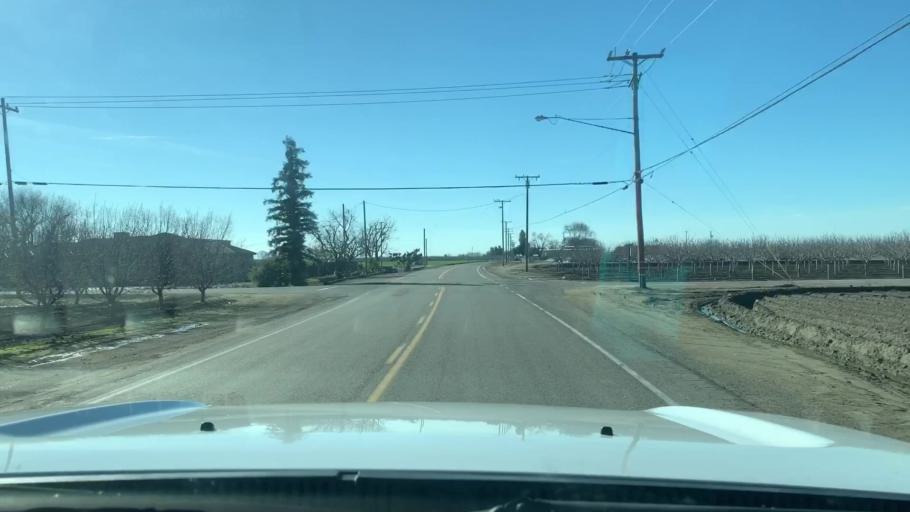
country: US
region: California
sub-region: Tulare County
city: Tulare
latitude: 36.1812
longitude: -119.4571
